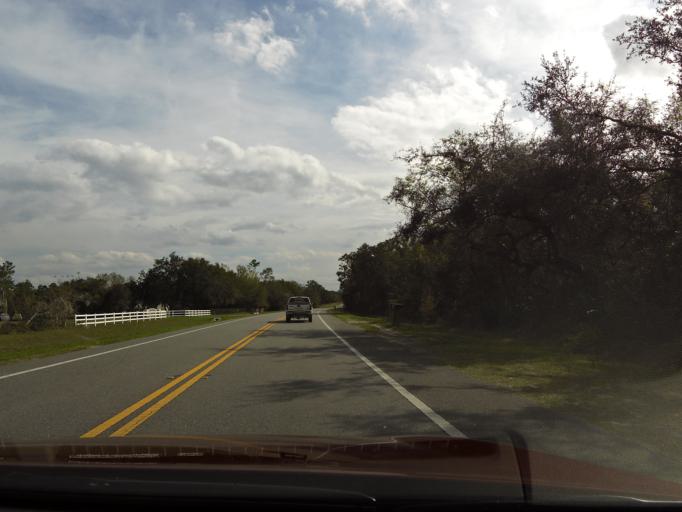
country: US
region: Florida
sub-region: Volusia County
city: De Leon Springs
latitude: 29.1823
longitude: -81.3046
